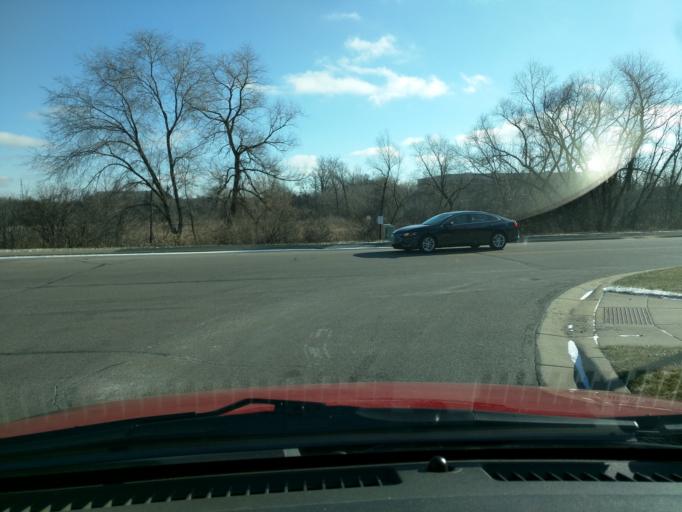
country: US
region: Minnesota
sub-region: Hennepin County
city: Eden Prairie
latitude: 44.8680
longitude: -93.4125
